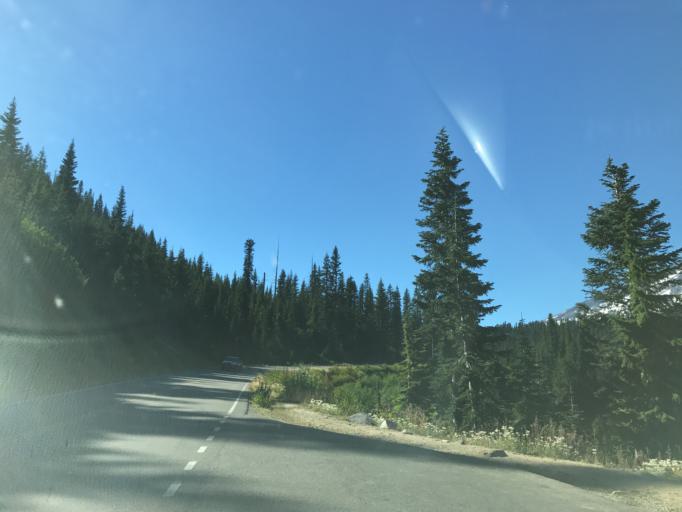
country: US
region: Washington
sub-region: Pierce County
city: Buckley
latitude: 46.7668
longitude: -121.7210
